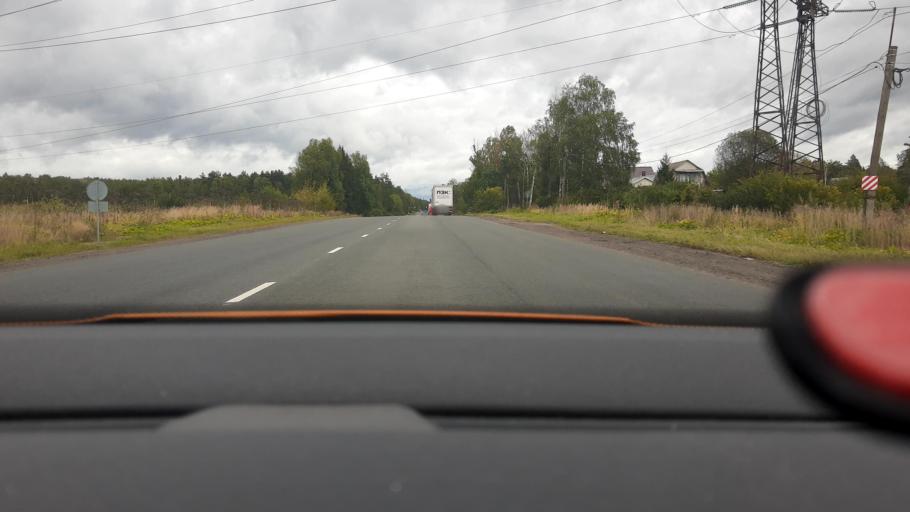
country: RU
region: Moskovskaya
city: Lesnoy
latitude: 56.0541
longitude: 37.9987
